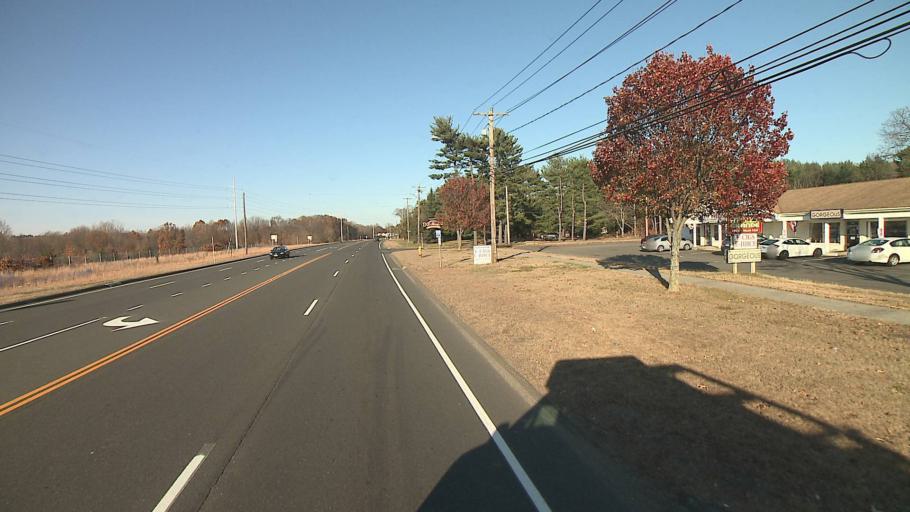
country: US
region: Connecticut
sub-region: New Haven County
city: Wallingford Center
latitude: 41.4224
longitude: -72.8394
